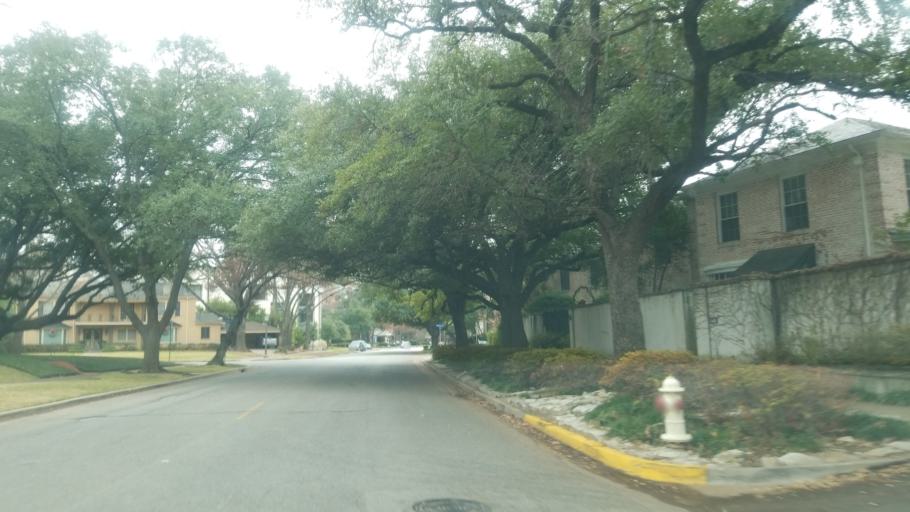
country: US
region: Texas
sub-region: Dallas County
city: Highland Park
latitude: 32.8244
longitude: -96.8122
